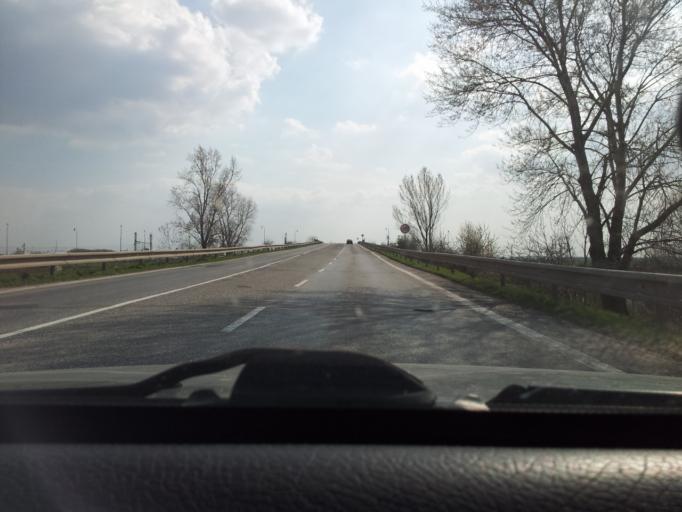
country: SK
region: Nitriansky
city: Tlmace
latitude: 48.2070
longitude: 18.5118
